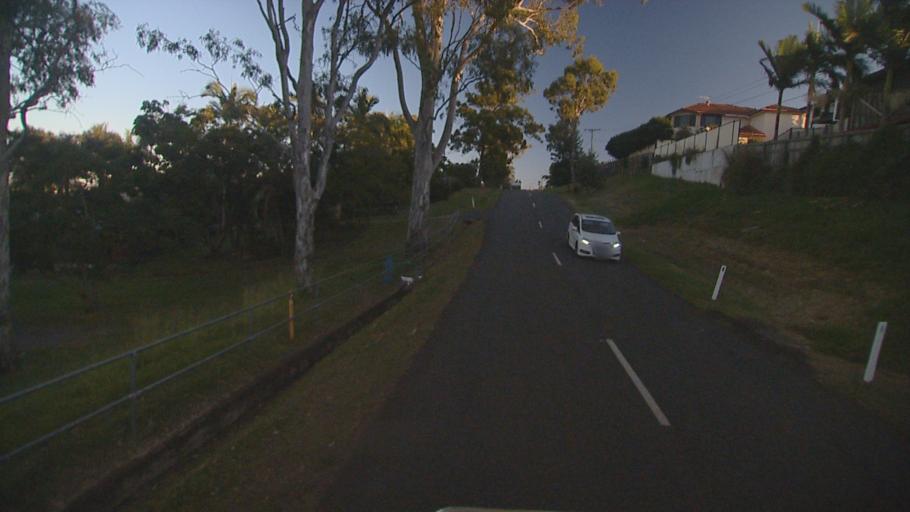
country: AU
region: Queensland
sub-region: Logan
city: Rochedale South
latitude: -27.6029
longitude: 153.1041
